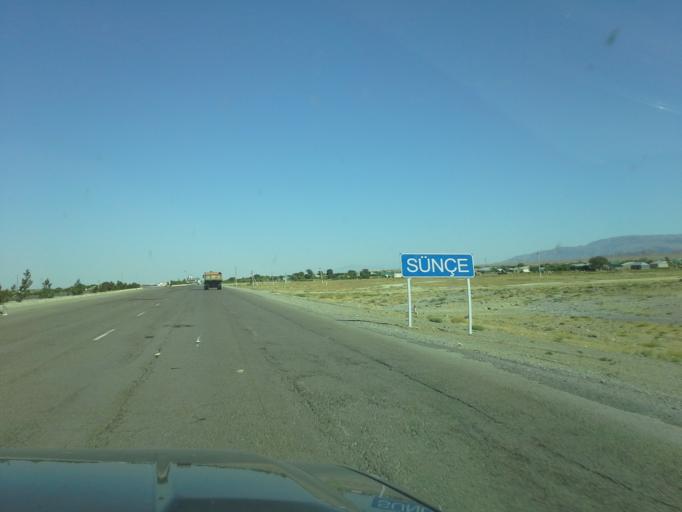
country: TM
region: Ahal
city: Baharly
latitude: 38.4994
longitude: 57.3012
